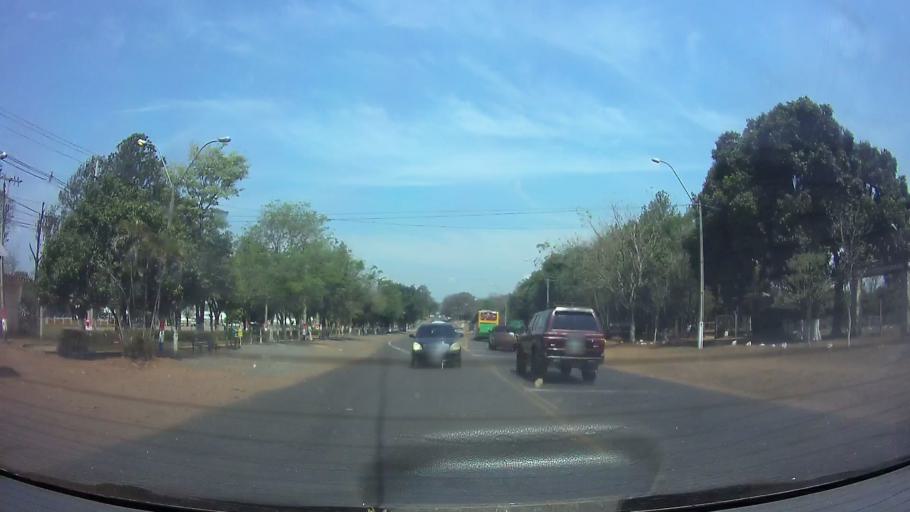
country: PY
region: Central
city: Capiata
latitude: -25.4027
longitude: -57.4635
